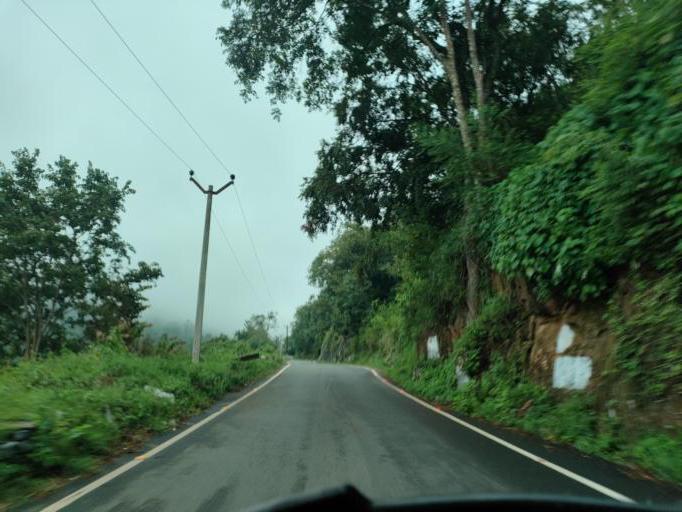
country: IN
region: Tamil Nadu
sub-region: Dindigul
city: Ayakudi
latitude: 10.3588
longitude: 77.5547
